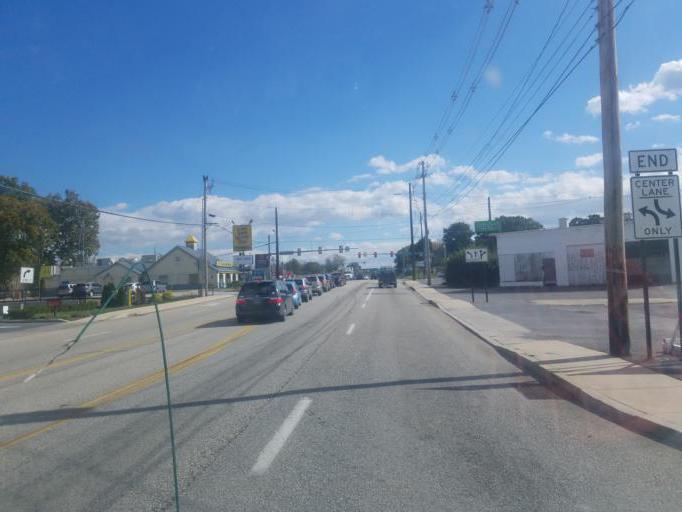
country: US
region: Pennsylvania
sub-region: Franklin County
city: Chambersburg
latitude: 39.9300
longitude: -77.6396
